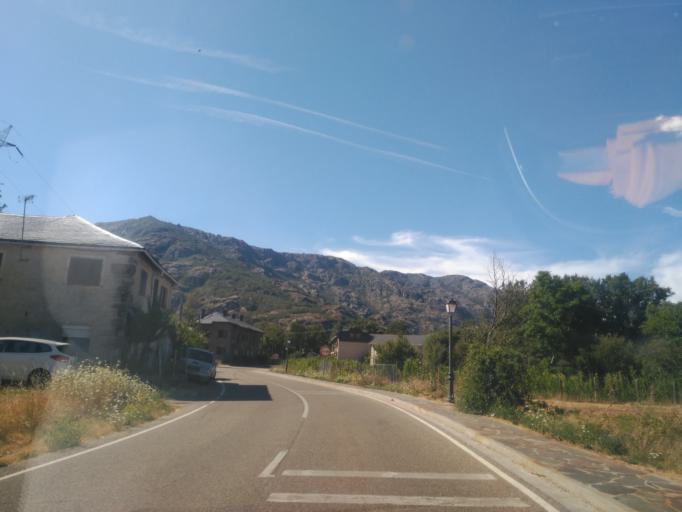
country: ES
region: Castille and Leon
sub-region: Provincia de Zamora
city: Cobreros
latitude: 42.1185
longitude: -6.7465
